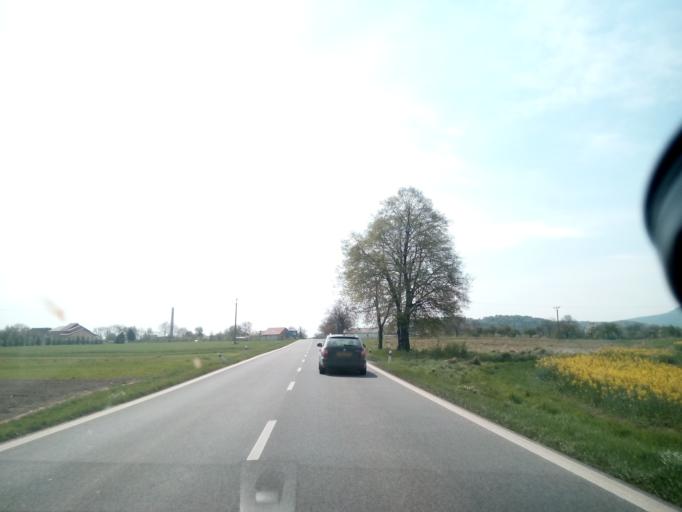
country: SK
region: Presovsky
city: Giraltovce
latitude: 49.0127
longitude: 21.5359
